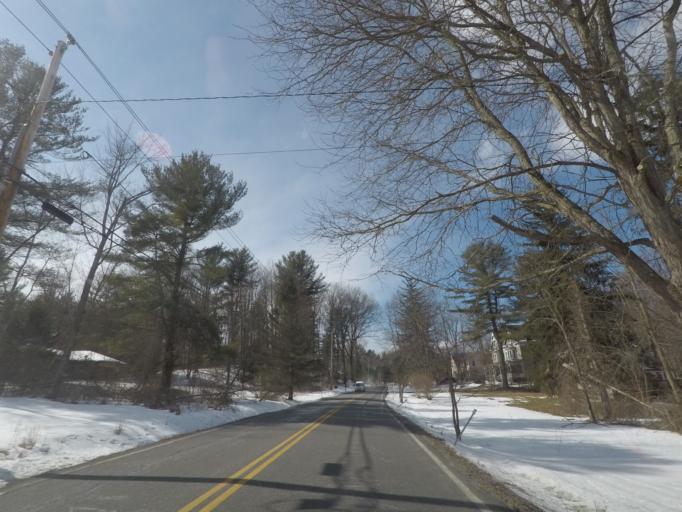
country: US
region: New York
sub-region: Albany County
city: Delmar
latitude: 42.6332
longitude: -73.8763
